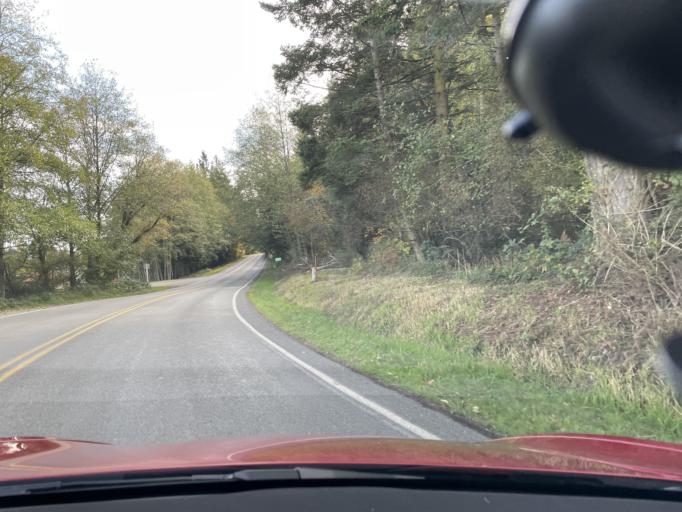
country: US
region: Washington
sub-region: San Juan County
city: Friday Harbor
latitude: 48.5397
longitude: -123.0343
